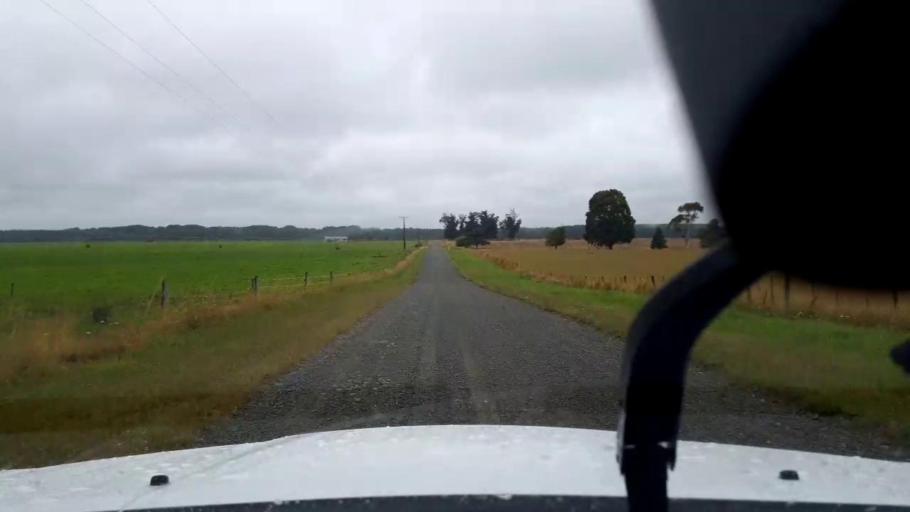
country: NZ
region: Canterbury
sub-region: Timaru District
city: Pleasant Point
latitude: -44.2462
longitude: 171.2009
